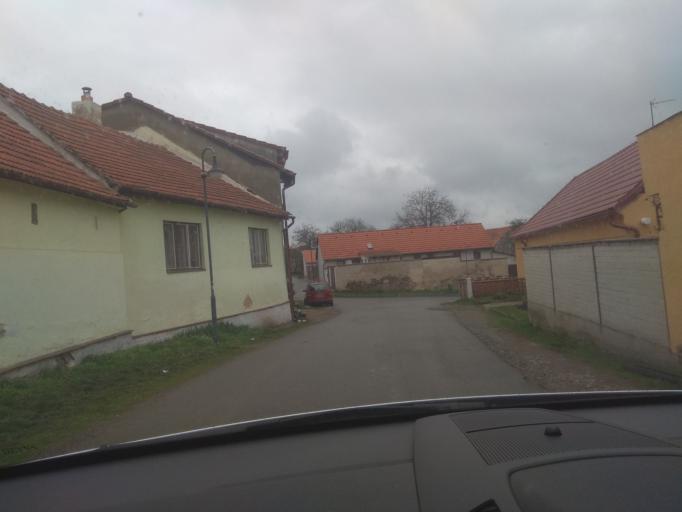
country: CZ
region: South Moravian
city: Zastavka
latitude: 49.1714
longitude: 16.3584
